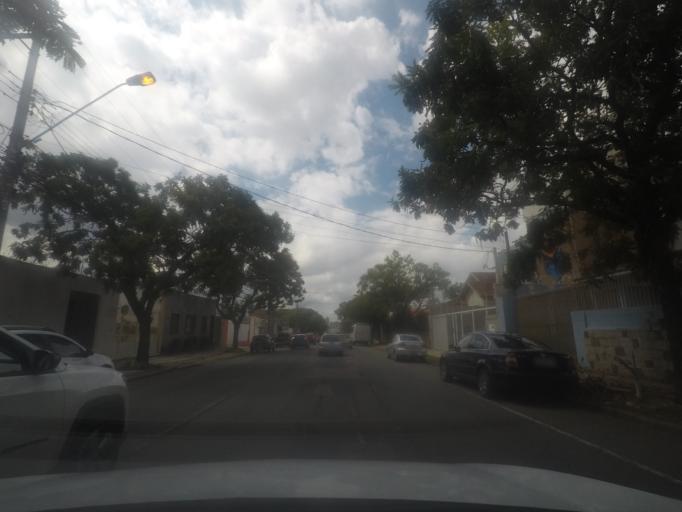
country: BR
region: Parana
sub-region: Curitiba
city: Curitiba
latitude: -25.4497
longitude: -49.2597
